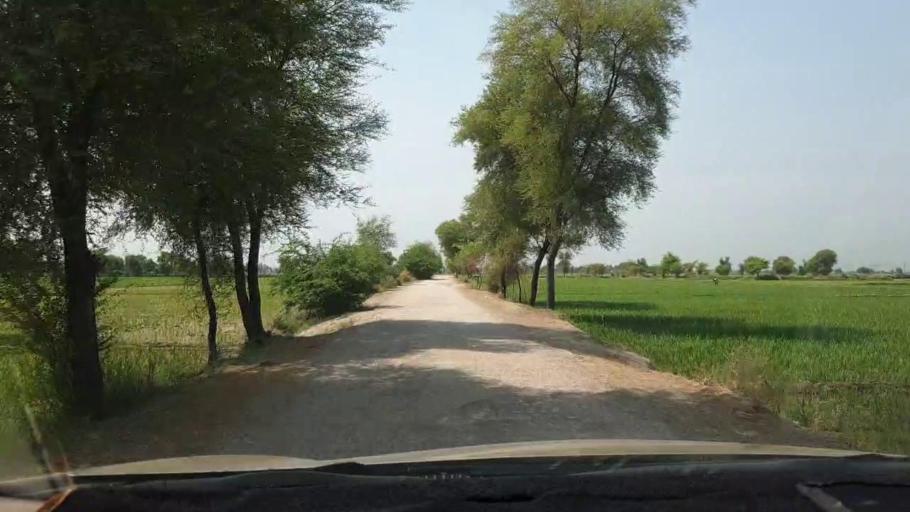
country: PK
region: Sindh
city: Naudero
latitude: 27.6434
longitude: 68.2747
